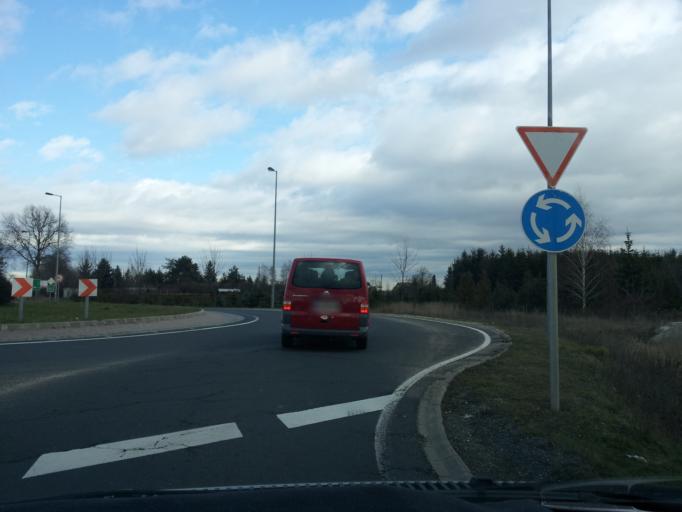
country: HU
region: Vas
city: Gencsapati
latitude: 47.2652
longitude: 16.6101
